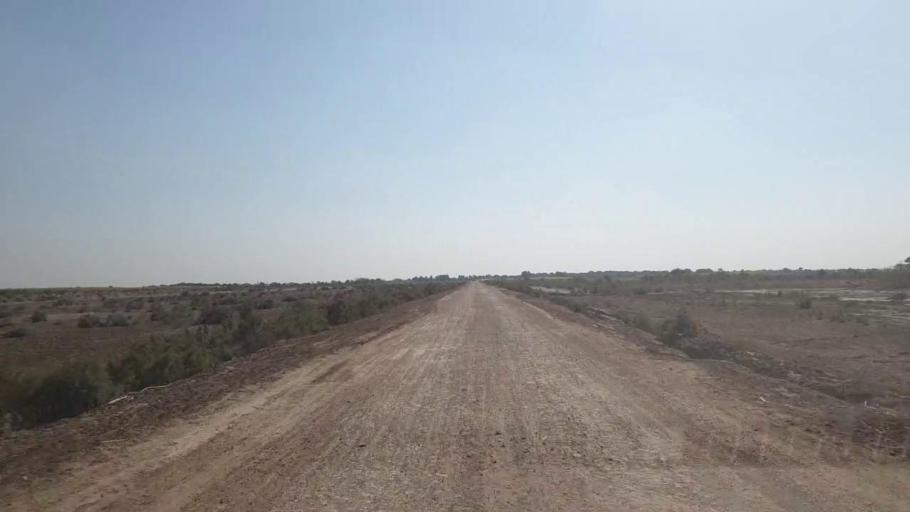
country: PK
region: Sindh
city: Chambar
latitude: 25.3258
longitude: 68.7399
